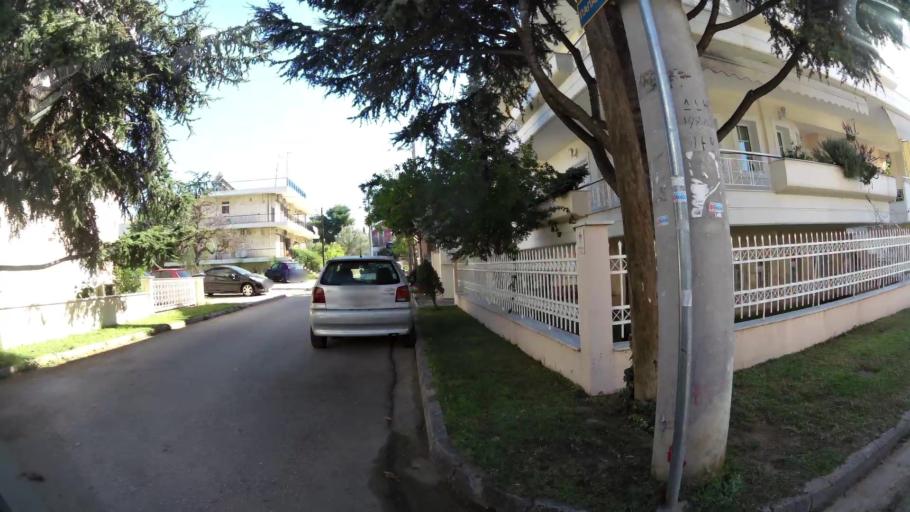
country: GR
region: Attica
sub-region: Nomarchia Athinas
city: Lykovrysi
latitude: 38.0755
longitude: 23.7903
